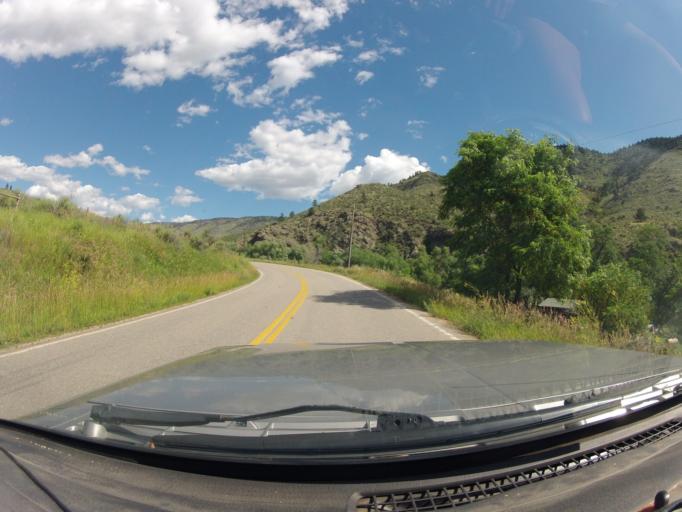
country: US
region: Colorado
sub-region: Larimer County
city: Laporte
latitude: 40.5459
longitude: -105.2838
